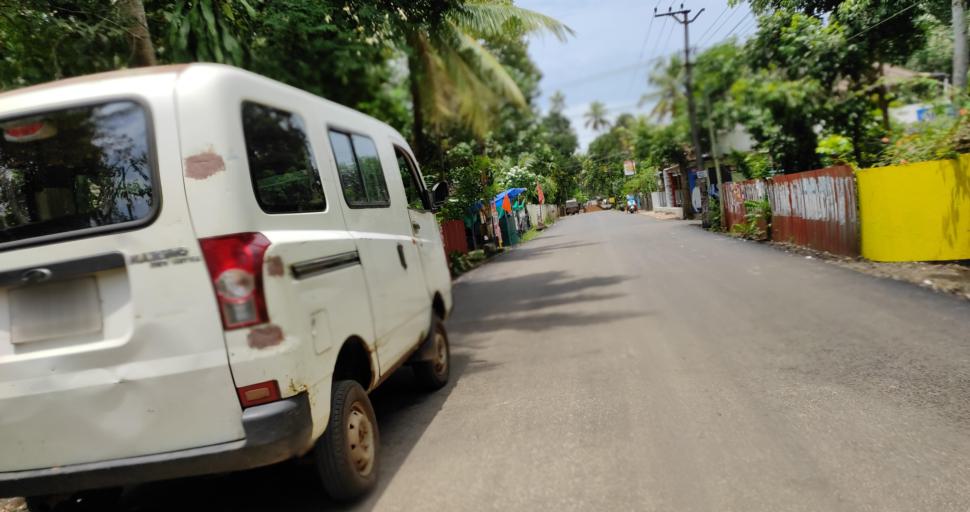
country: IN
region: Kerala
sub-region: Alappuzha
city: Vayalar
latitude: 9.6877
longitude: 76.3134
